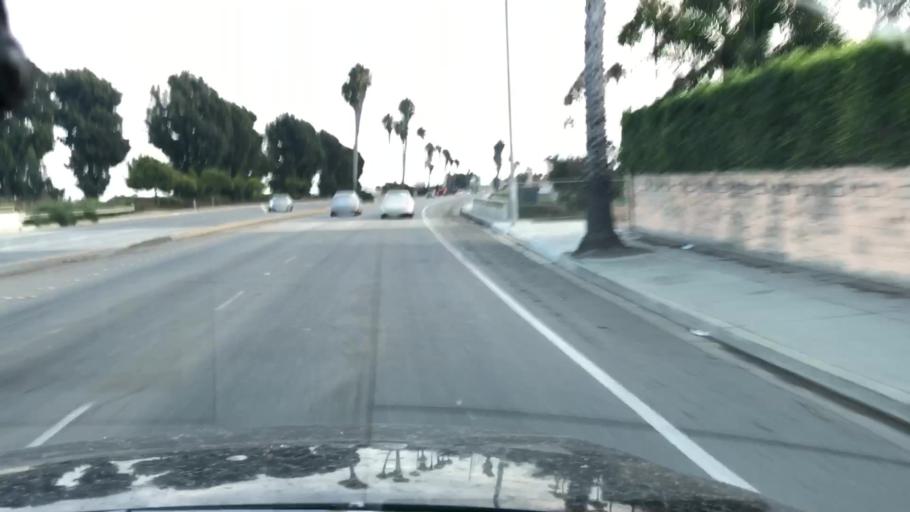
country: US
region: California
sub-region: Ventura County
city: Ventura
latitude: 34.2531
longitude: -119.2592
